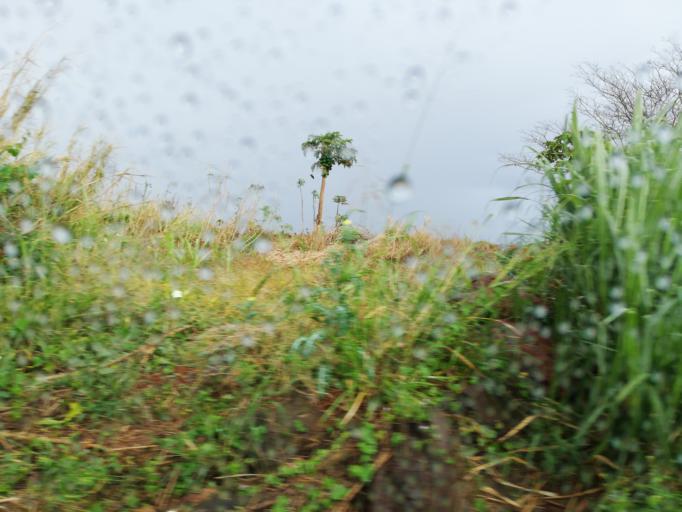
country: MU
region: Pamplemousses
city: Long Mountain
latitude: -20.1288
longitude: 57.5660
